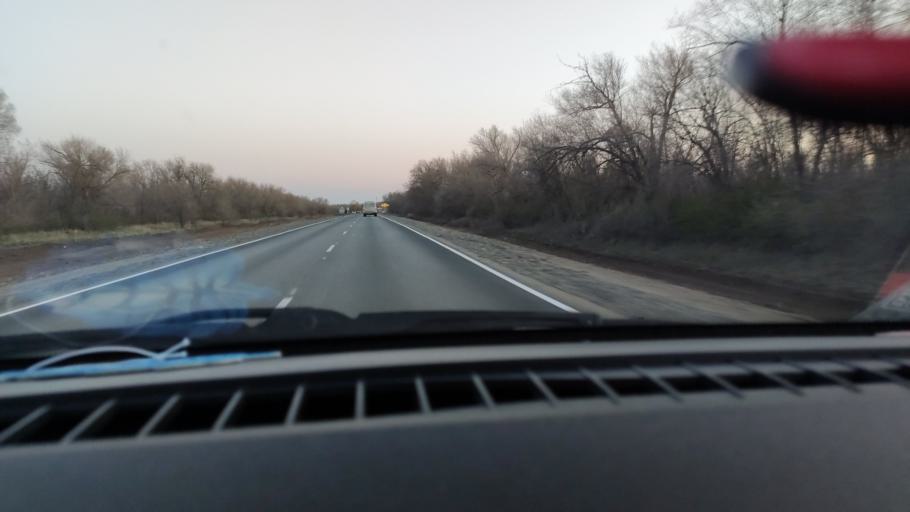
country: RU
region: Saratov
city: Krasnoarmeysk
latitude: 51.1214
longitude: 45.9574
